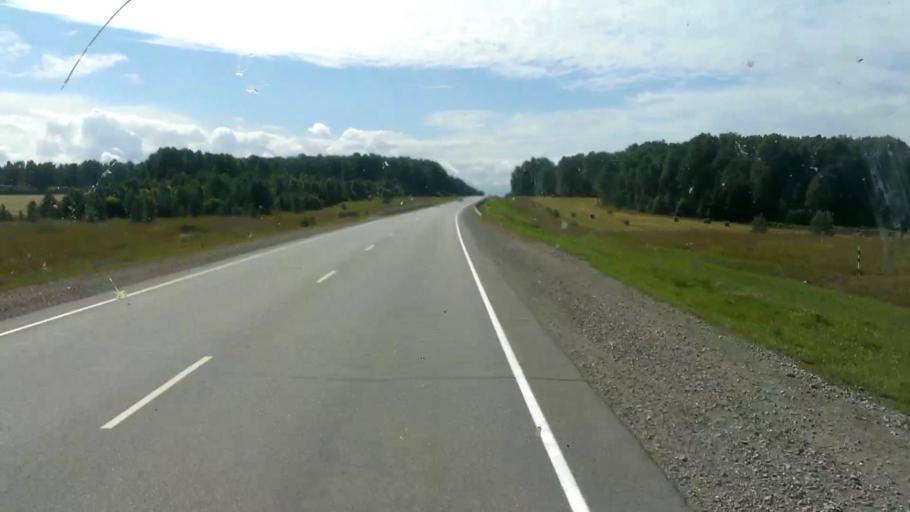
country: RU
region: Altai Krai
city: Troitskoye
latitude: 53.0595
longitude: 84.6954
